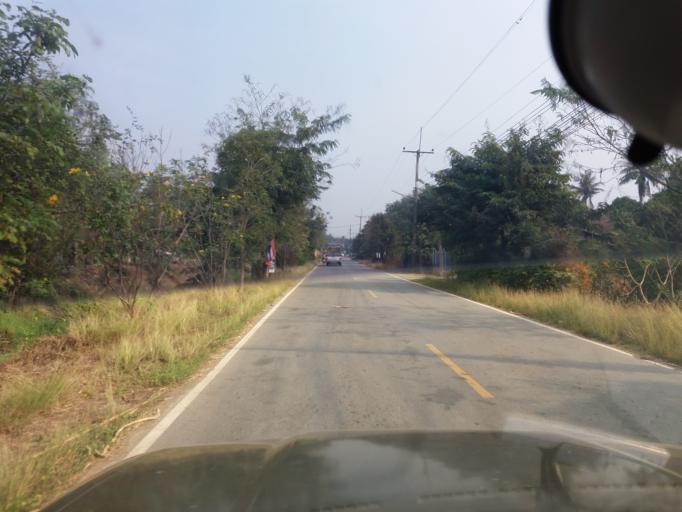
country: TH
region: Suphan Buri
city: Doem Bang Nang Buat
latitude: 14.9020
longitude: 100.1917
